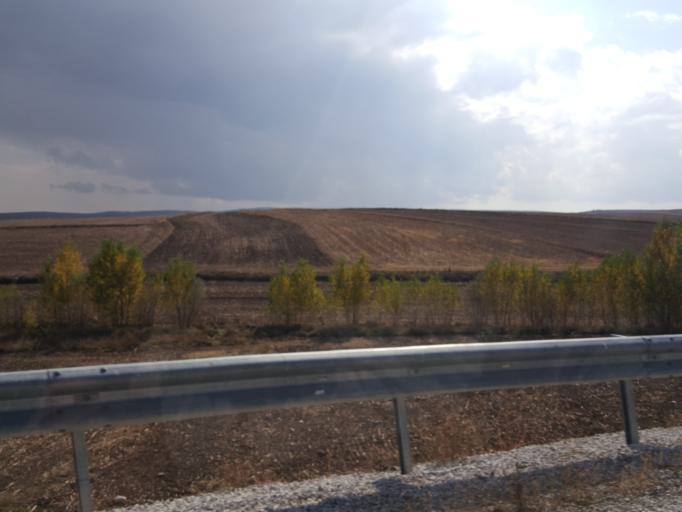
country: TR
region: Corum
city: Bogazkale
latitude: 40.1554
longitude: 34.6878
